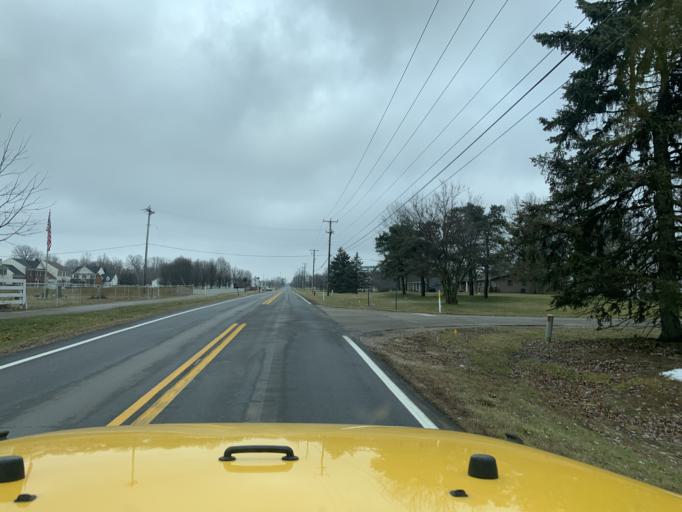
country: US
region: Ohio
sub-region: Franklin County
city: New Albany
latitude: 40.0976
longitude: -82.8030
